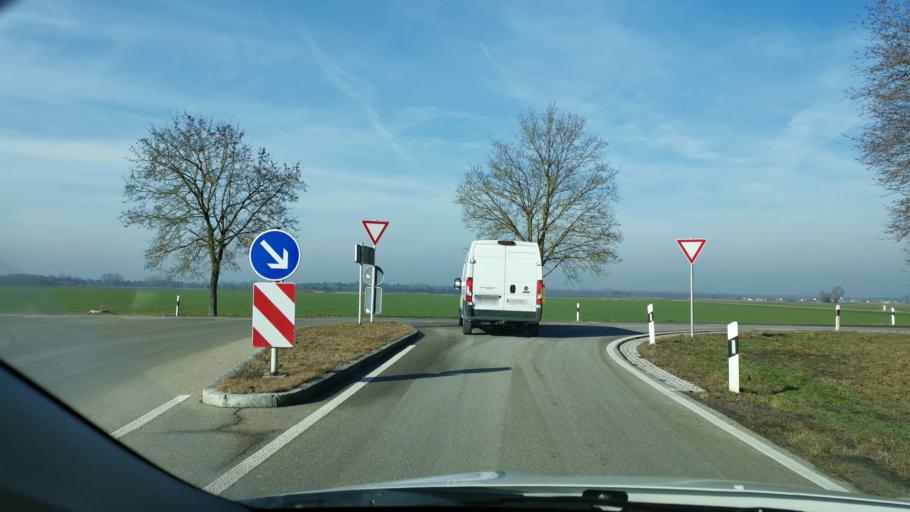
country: DE
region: Bavaria
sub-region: Swabia
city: Munster
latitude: 48.6415
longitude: 10.9192
